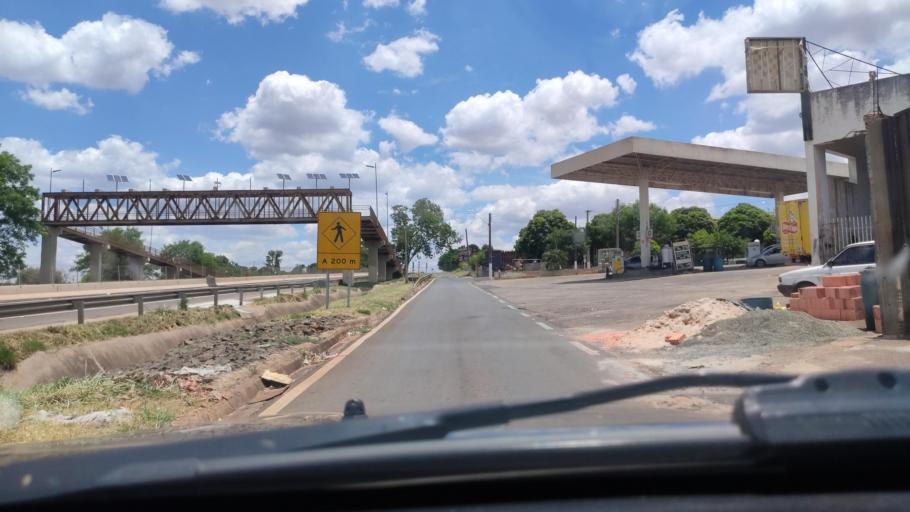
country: BR
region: Sao Paulo
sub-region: Duartina
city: Duartina
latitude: -22.6977
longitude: -49.4295
